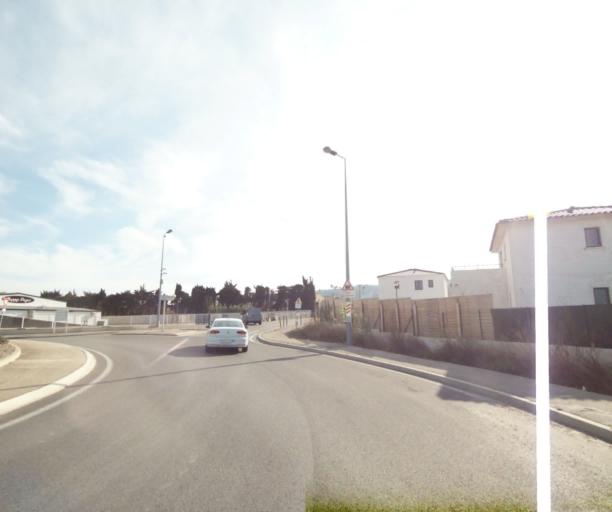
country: FR
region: Provence-Alpes-Cote d'Azur
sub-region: Departement des Bouches-du-Rhone
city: Chateauneuf-les-Martigues
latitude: 43.3903
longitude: 5.1619
